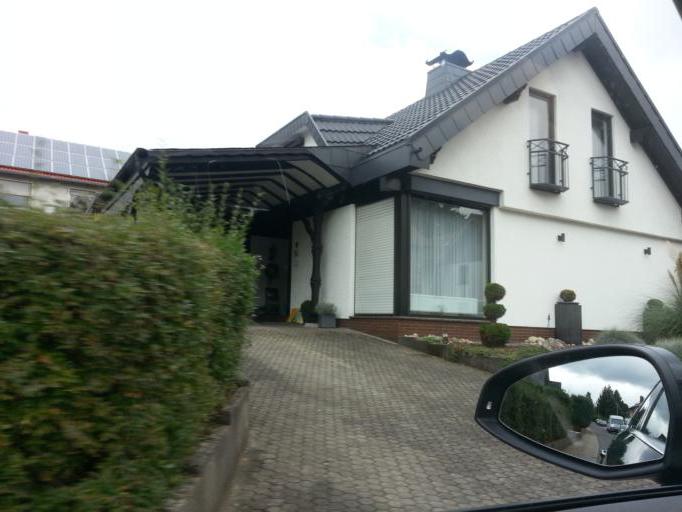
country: DE
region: Saarland
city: Bexbach
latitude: 49.3551
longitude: 7.2539
